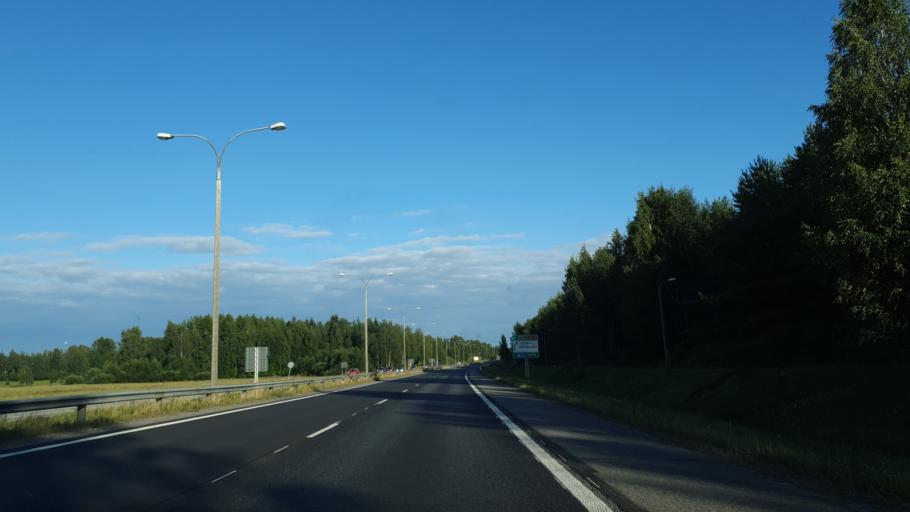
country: FI
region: North Karelia
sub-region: Joensuu
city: Joensuu
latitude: 62.6226
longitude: 29.7182
